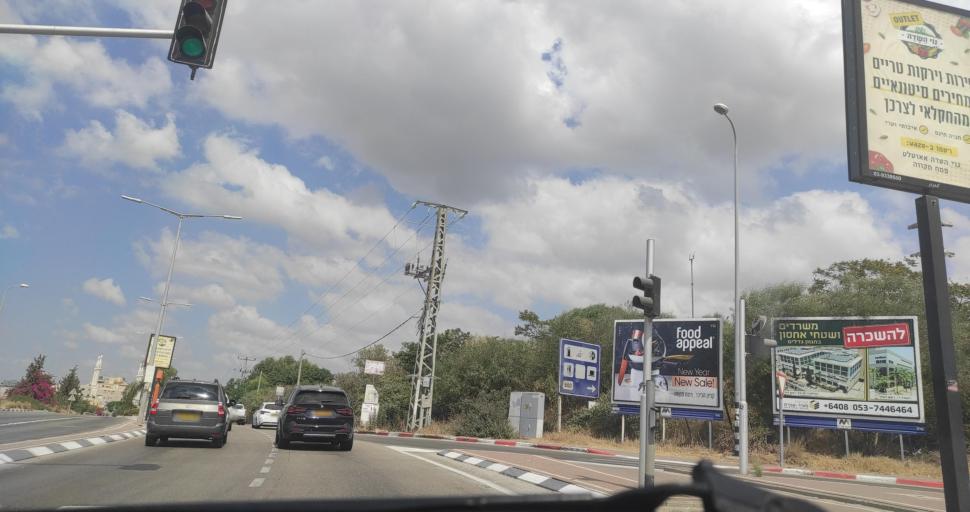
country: IL
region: Central District
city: Kafr Qasim
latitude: 32.1089
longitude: 34.9631
